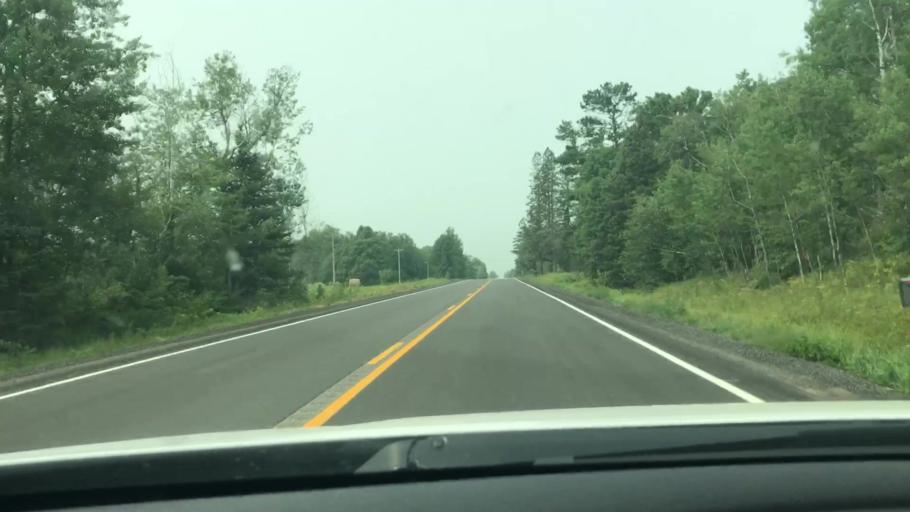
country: US
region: Minnesota
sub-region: Itasca County
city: Cohasset
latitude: 47.3590
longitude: -93.8591
